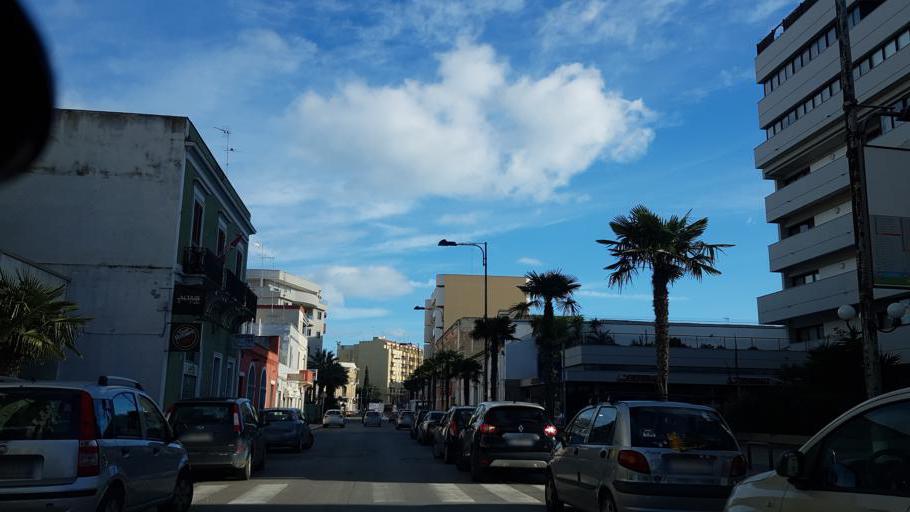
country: IT
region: Apulia
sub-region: Provincia di Brindisi
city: Brindisi
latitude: 40.6350
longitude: 17.9354
